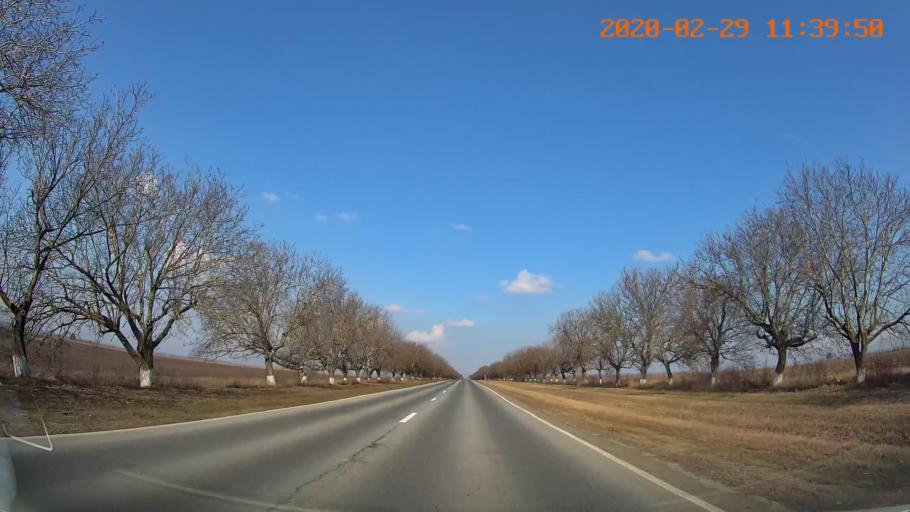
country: MD
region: Rezina
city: Saharna
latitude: 47.6463
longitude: 29.0227
